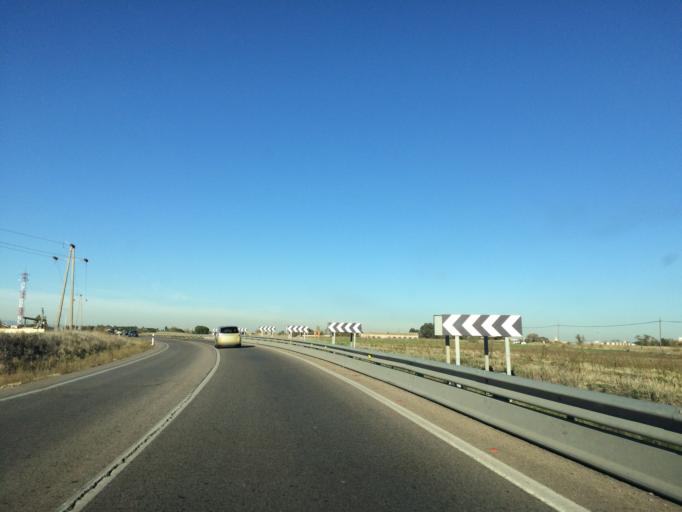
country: ES
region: Madrid
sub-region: Provincia de Madrid
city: Serranillos del Valle
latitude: 40.1997
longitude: -3.8711
